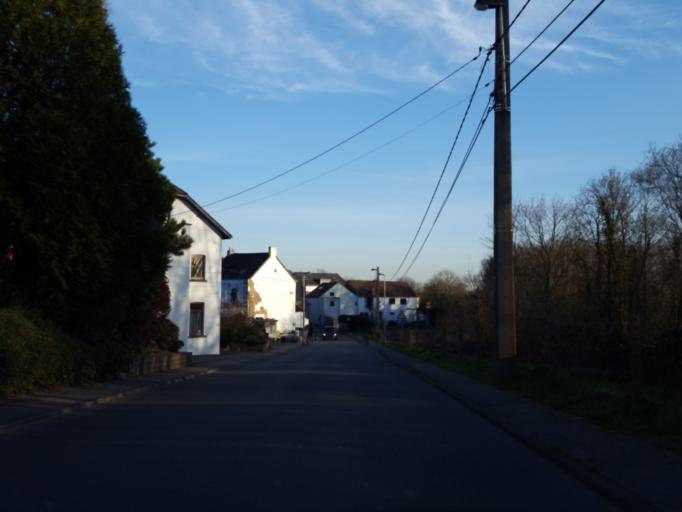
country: BE
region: Wallonia
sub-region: Province du Brabant Wallon
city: Mont-Saint-Guibert
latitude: 50.6422
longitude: 4.6093
